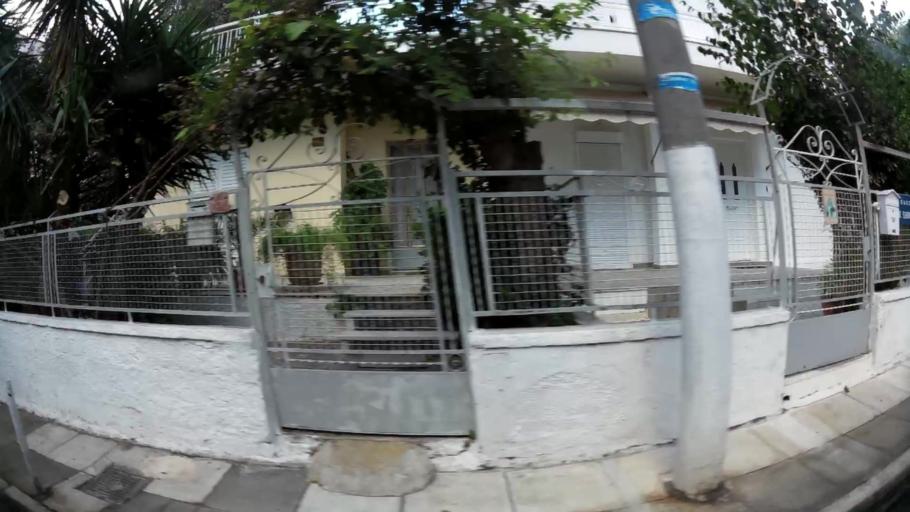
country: GR
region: Attica
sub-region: Nomarchia Athinas
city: Marousi
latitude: 38.0476
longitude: 23.8118
